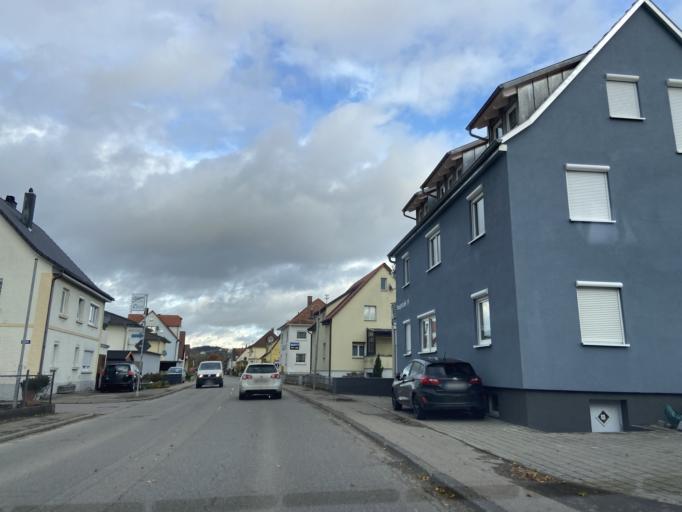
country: DE
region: Baden-Wuerttemberg
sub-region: Tuebingen Region
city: Inzigkofen
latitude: 48.0790
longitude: 9.1991
